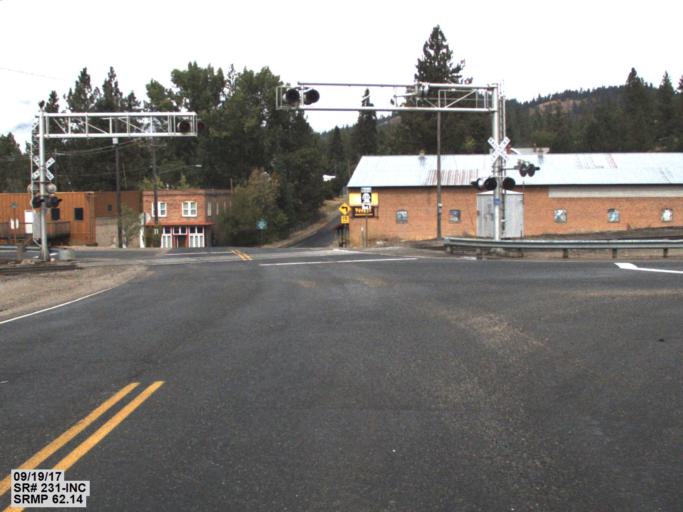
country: US
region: Washington
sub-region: Stevens County
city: Chewelah
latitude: 48.0566
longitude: -117.7413
